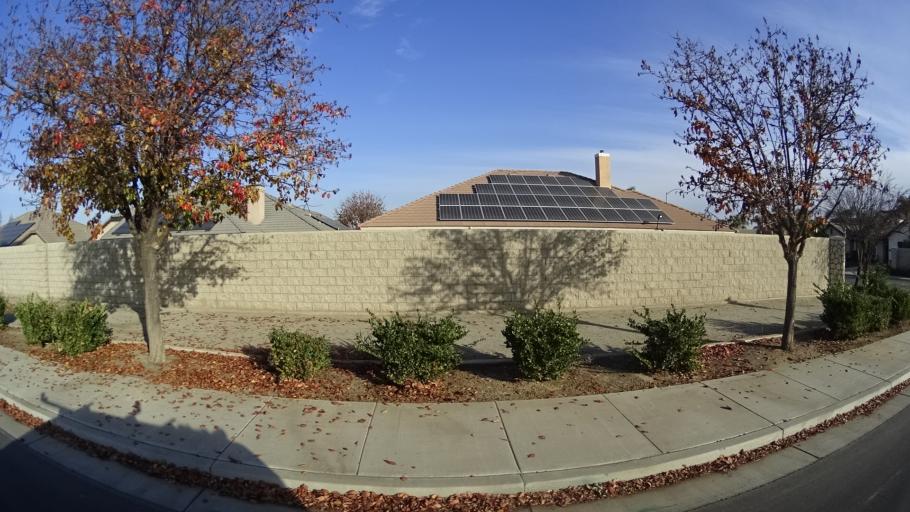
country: US
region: California
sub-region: Kern County
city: Rosedale
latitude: 35.4053
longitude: -119.1420
